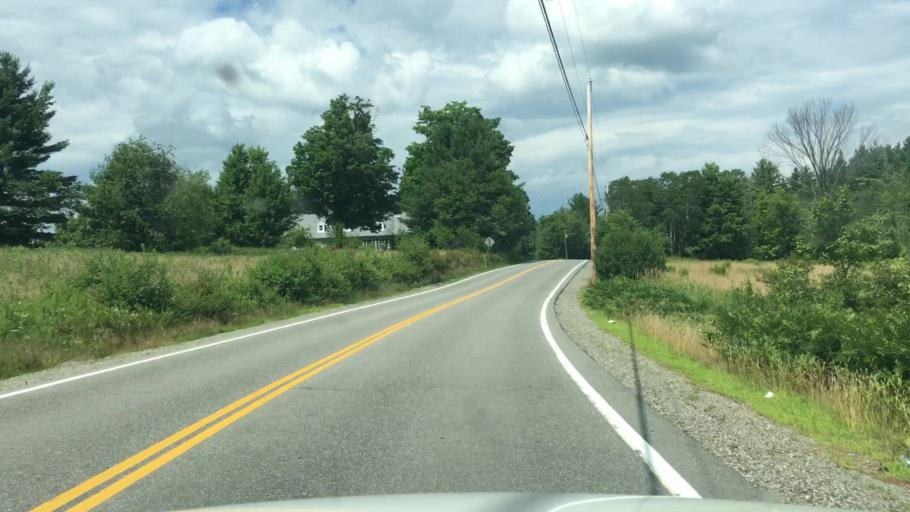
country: US
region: New Hampshire
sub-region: Coos County
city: Whitefield
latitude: 44.3087
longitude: -71.6590
